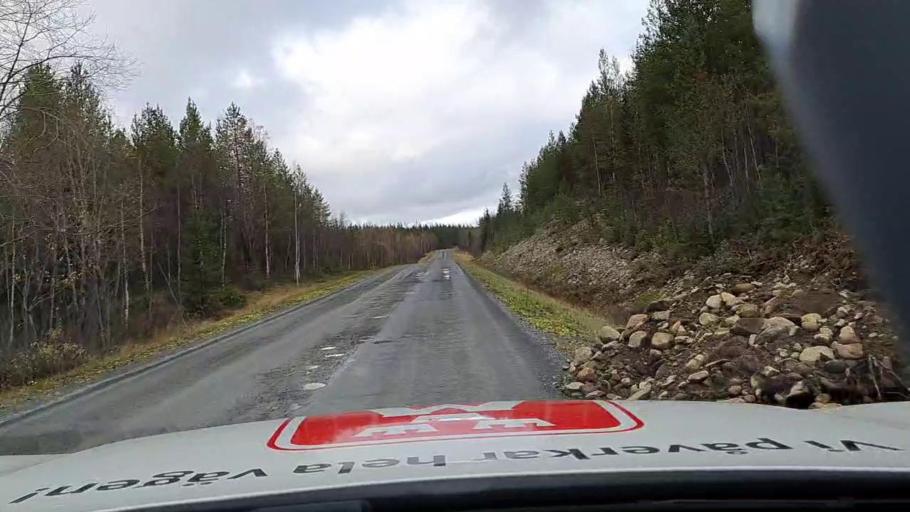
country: SE
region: Jaemtland
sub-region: Krokoms Kommun
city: Valla
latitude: 63.0677
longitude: 13.9590
